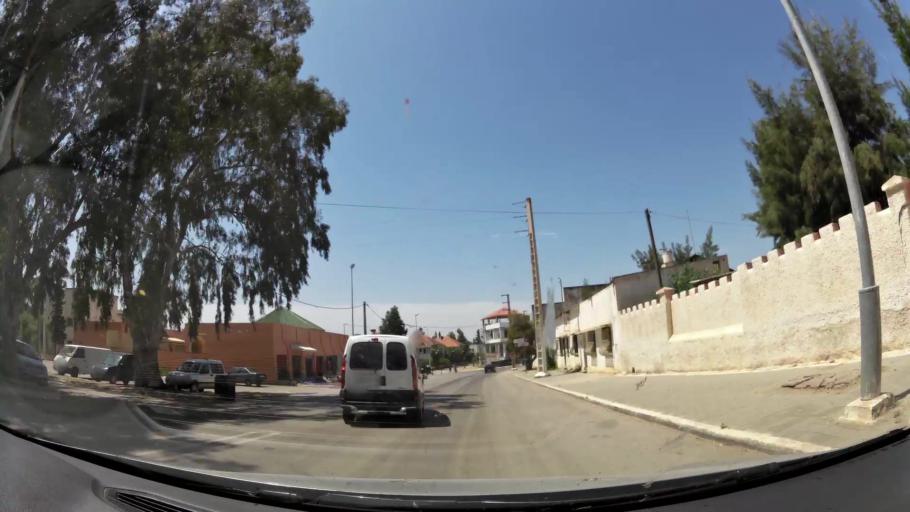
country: MA
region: Rabat-Sale-Zemmour-Zaer
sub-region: Khemisset
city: Khemisset
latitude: 33.8248
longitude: -6.0628
